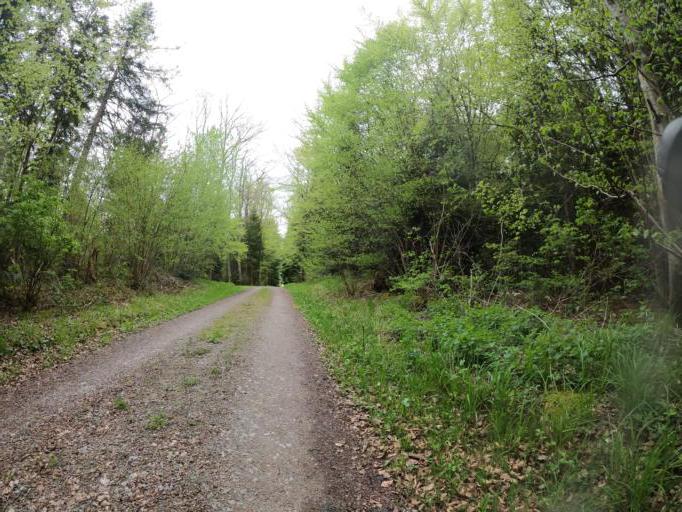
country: DE
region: Baden-Wuerttemberg
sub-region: Karlsruhe Region
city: Rohrdorf
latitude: 48.5559
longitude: 8.6915
